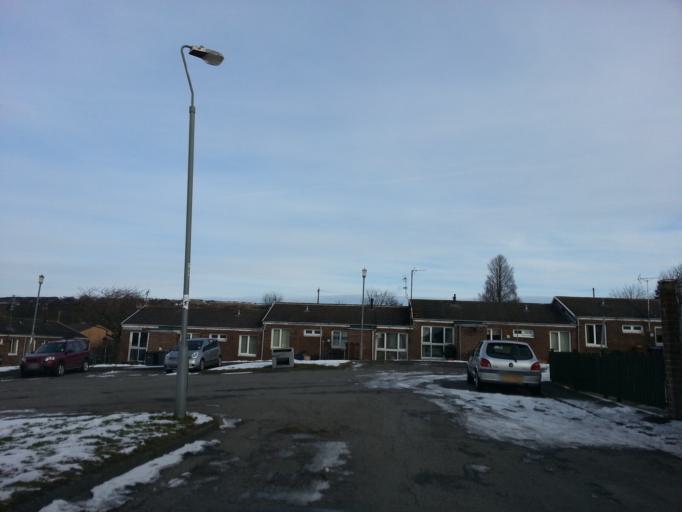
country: GB
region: England
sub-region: County Durham
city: Crook
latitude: 54.7107
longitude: -1.7359
